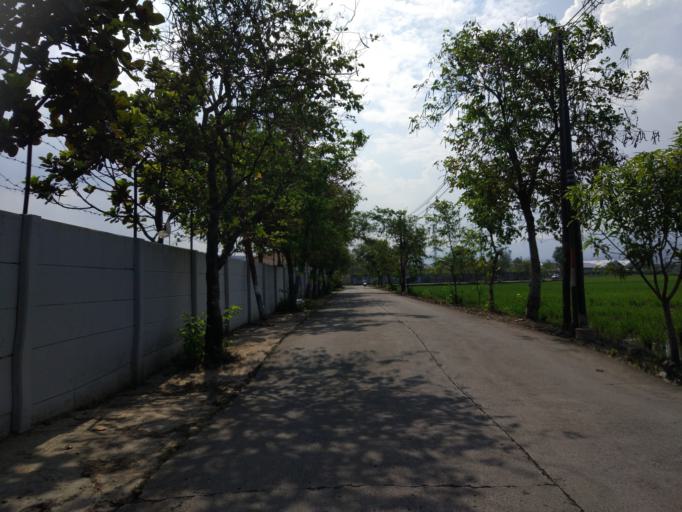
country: ID
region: West Java
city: Cileunyi
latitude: -6.9329
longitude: 107.7063
